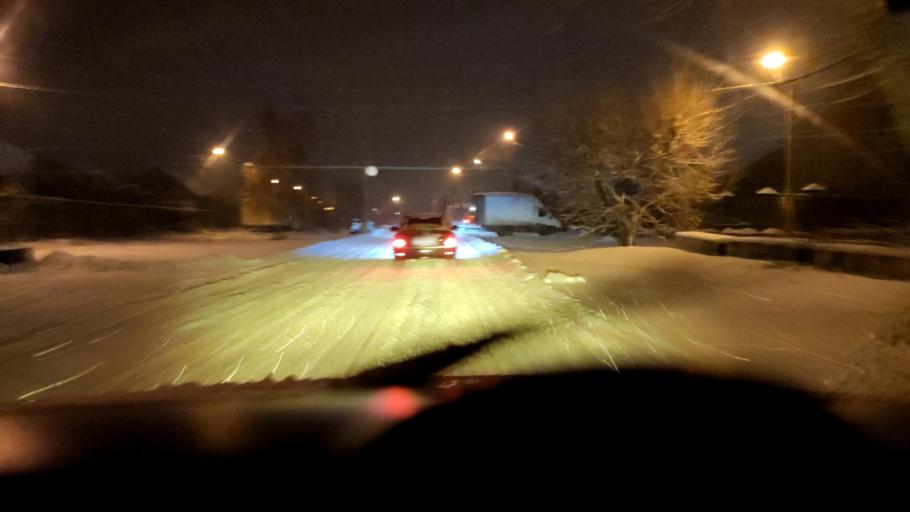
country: RU
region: Voronezj
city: Pridonskoy
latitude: 51.6733
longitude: 39.0772
